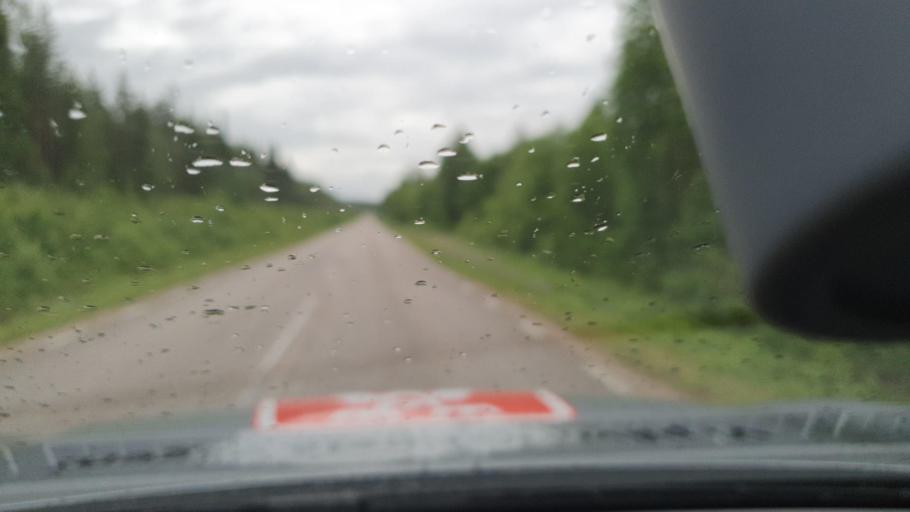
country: SE
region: Norrbotten
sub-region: Overkalix Kommun
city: OEverkalix
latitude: 66.3960
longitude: 22.7899
